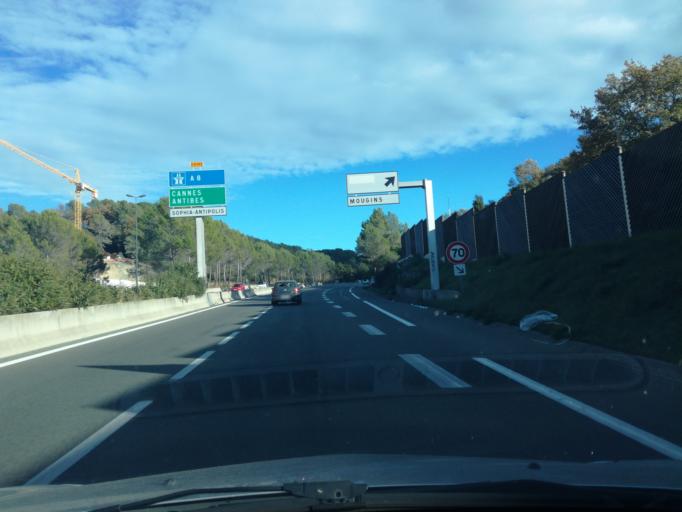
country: FR
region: Provence-Alpes-Cote d'Azur
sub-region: Departement des Alpes-Maritimes
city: Mouans-Sartoux
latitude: 43.6077
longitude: 6.9830
